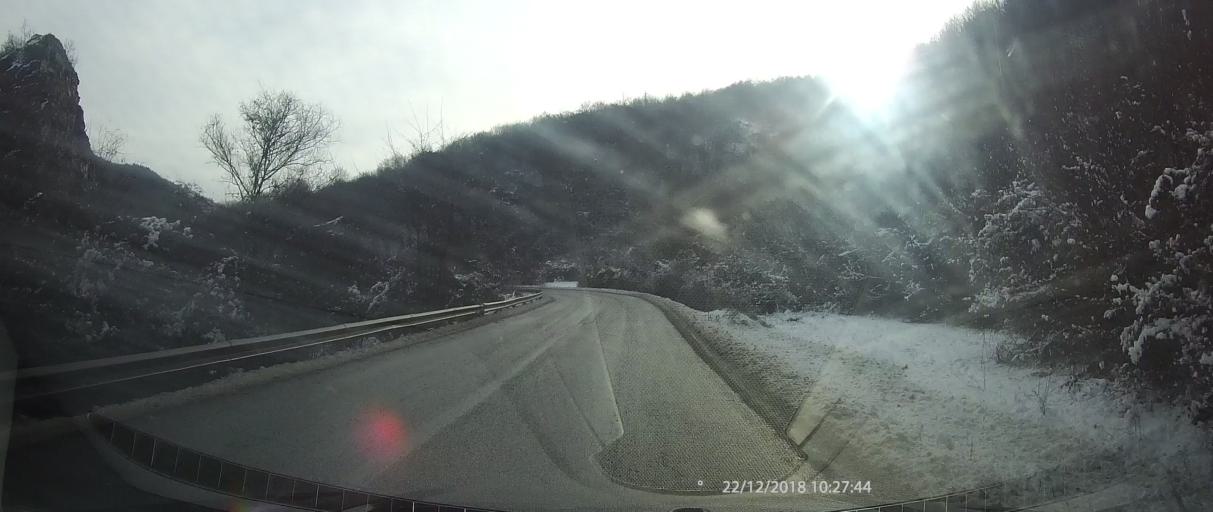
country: MK
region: Kriva Palanka
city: Kriva Palanka
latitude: 42.2297
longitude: 22.3735
